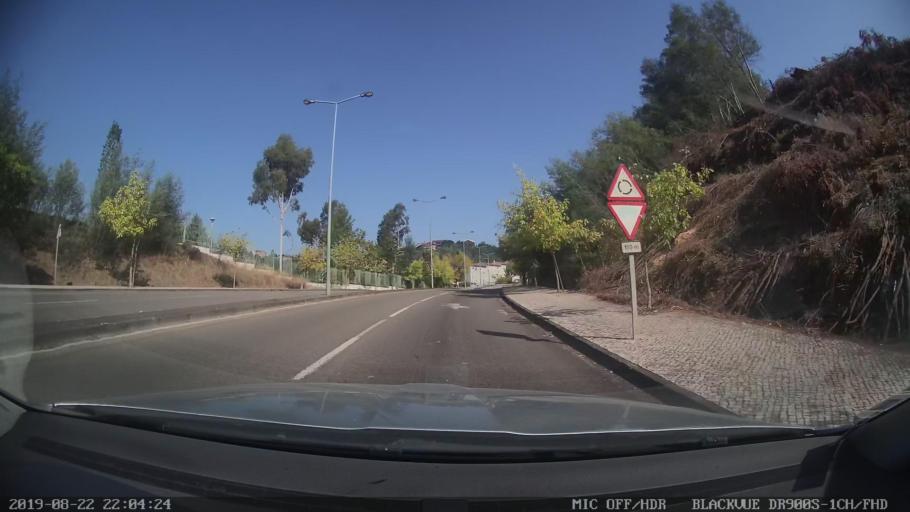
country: PT
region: Coimbra
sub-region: Coimbra
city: Coimbra
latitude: 40.2082
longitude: -8.4012
